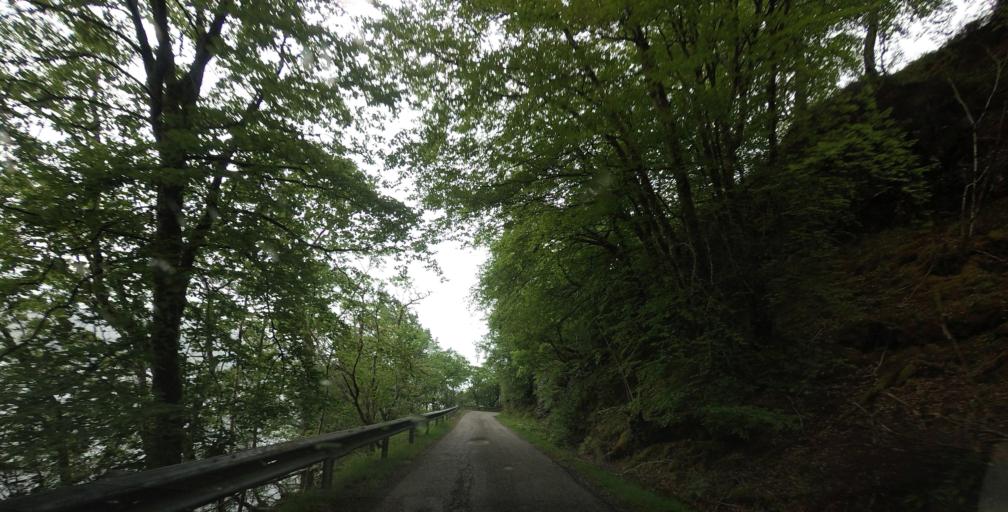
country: GB
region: Scotland
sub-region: Highland
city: Fort William
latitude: 56.7903
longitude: -5.1761
